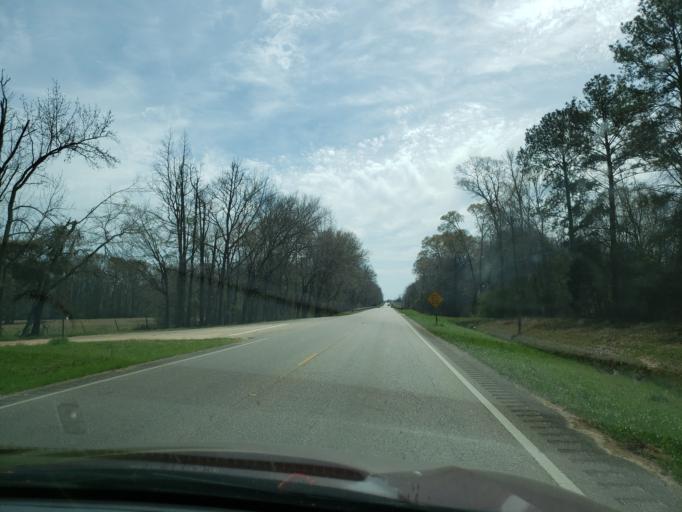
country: US
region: Alabama
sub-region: Dallas County
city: Selma
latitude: 32.4520
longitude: -87.0792
